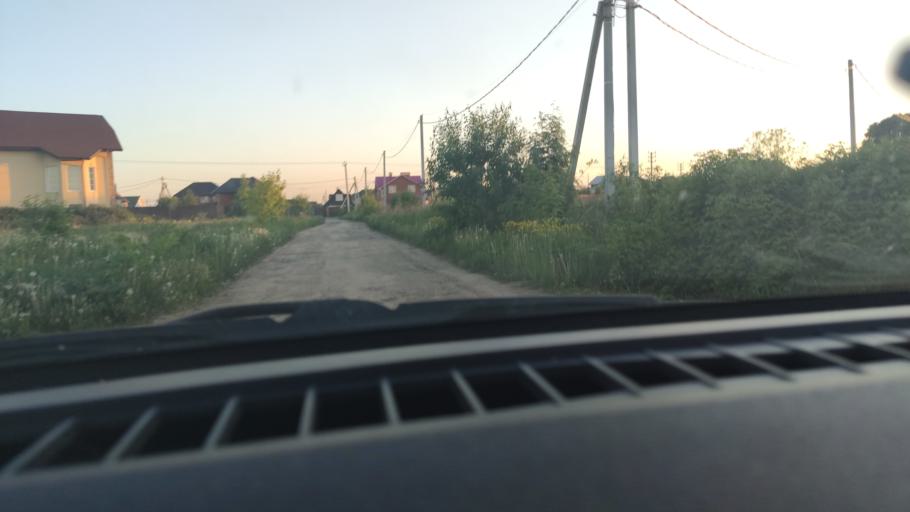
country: RU
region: Perm
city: Kultayevo
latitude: 57.9027
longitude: 55.9736
